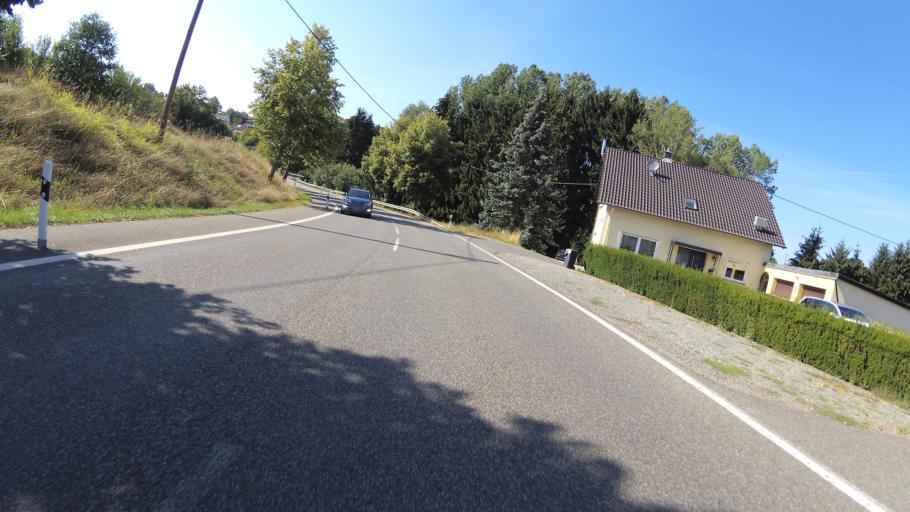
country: DE
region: Saarland
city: Eppelborn
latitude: 49.3830
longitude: 6.9619
